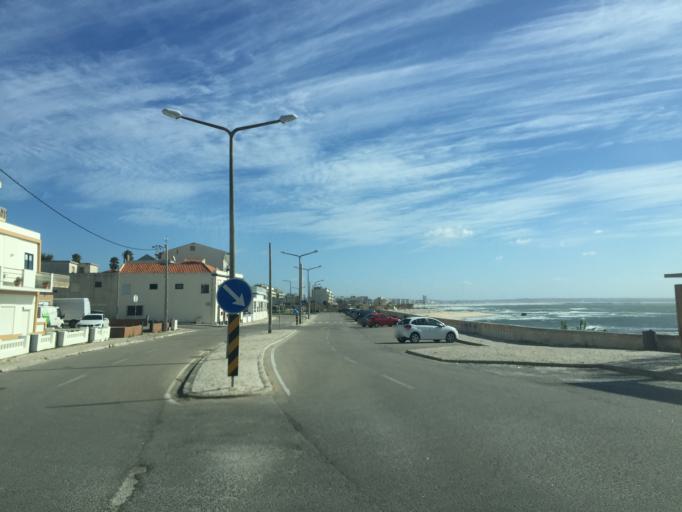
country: PT
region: Coimbra
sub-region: Figueira da Foz
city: Buarcos
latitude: 40.1771
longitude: -8.8993
